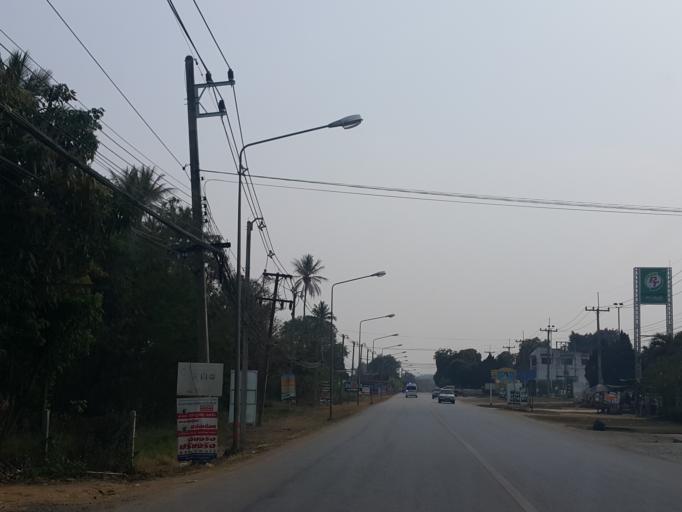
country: TH
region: Chiang Mai
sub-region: Amphoe Chiang Dao
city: Chiang Dao
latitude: 19.3624
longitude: 98.9643
